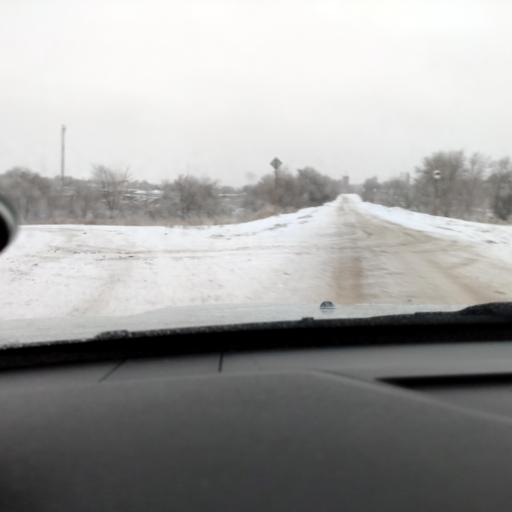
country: RU
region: Samara
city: Smyshlyayevka
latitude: 53.2423
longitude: 50.4809
